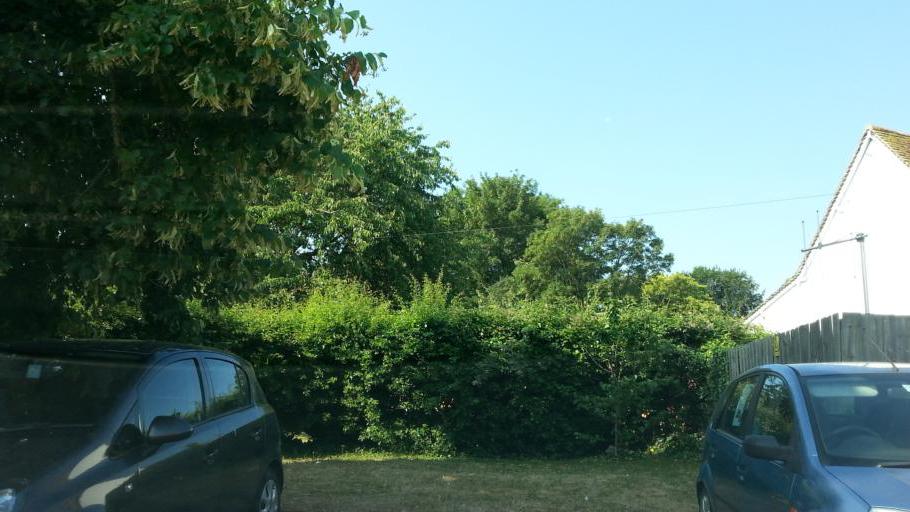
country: GB
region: England
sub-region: Cambridgeshire
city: Brampton
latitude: 52.3239
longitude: -0.2273
